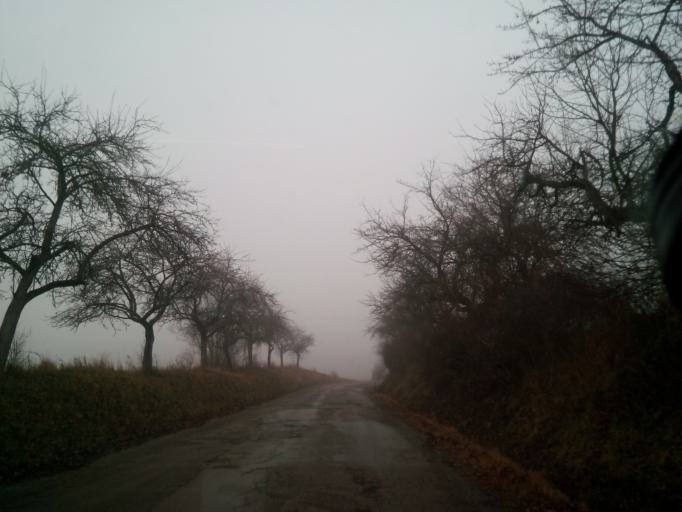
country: SK
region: Presovsky
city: Spisske Podhradie
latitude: 49.0308
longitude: 20.7977
